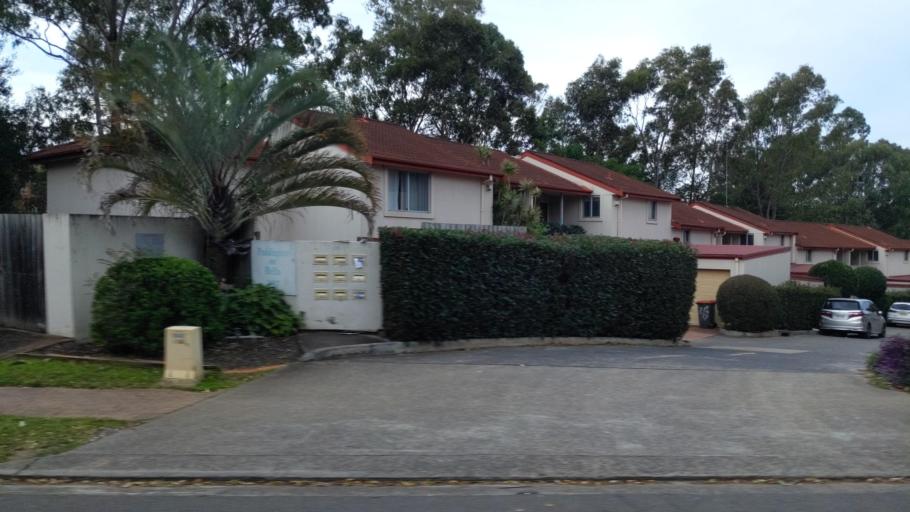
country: AU
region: New South Wales
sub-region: The Hills Shire
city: Baulkham Hills
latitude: -33.7430
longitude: 150.9583
